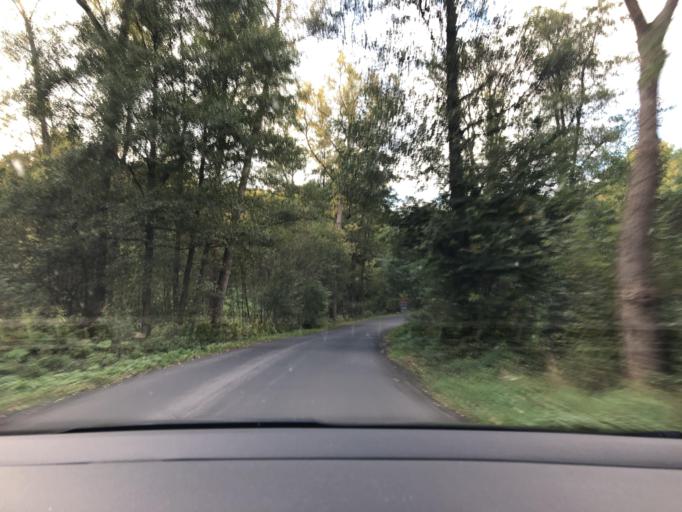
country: CZ
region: Ustecky
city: Velke Brezno
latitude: 50.6428
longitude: 14.1498
